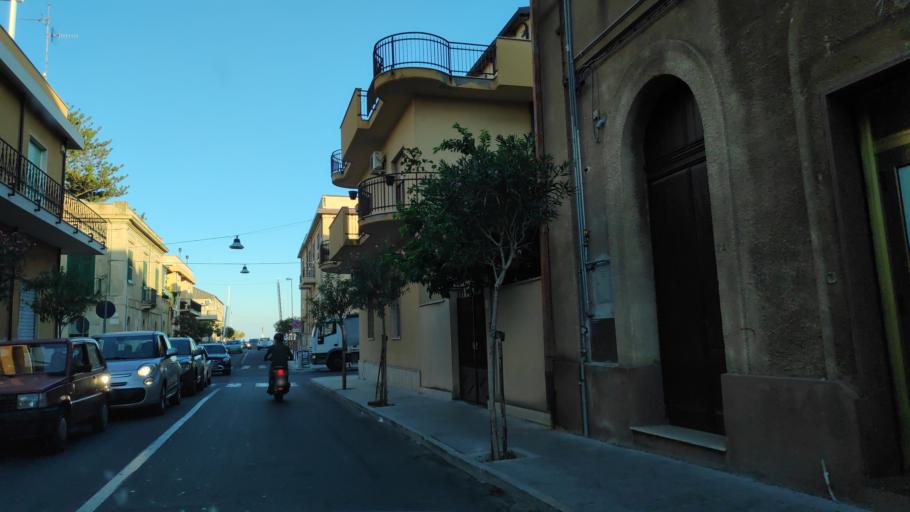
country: IT
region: Calabria
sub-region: Provincia di Reggio Calabria
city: Locri
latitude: 38.2357
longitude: 16.2658
